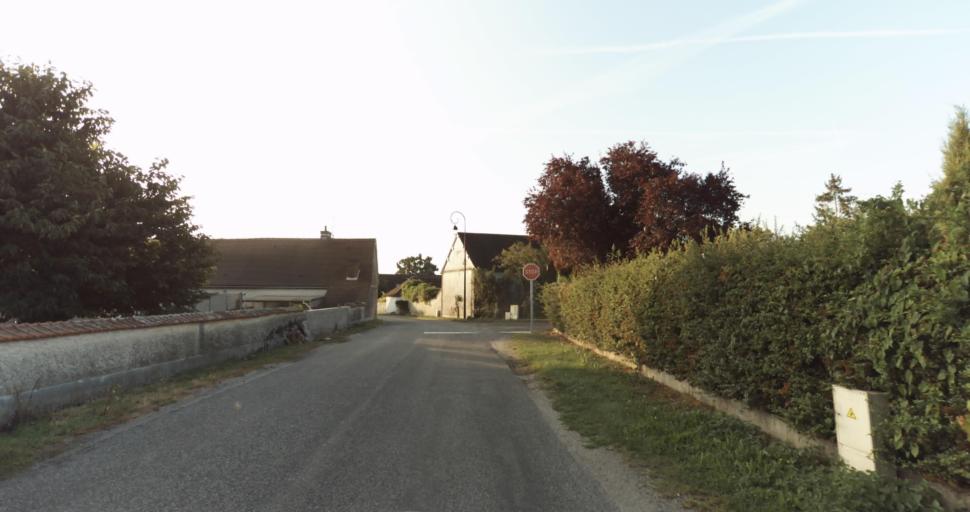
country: FR
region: Haute-Normandie
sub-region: Departement de l'Eure
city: Marcilly-sur-Eure
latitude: 48.7862
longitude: 1.3410
